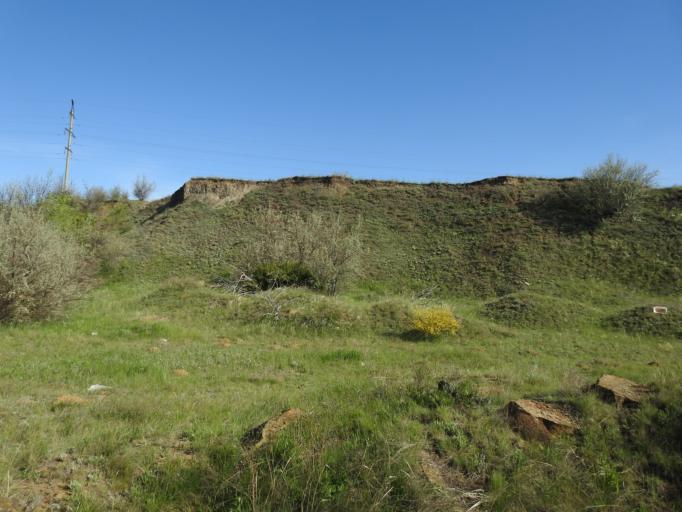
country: RU
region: Saratov
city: Krasnyy Oktyabr'
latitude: 51.6279
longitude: 45.7376
